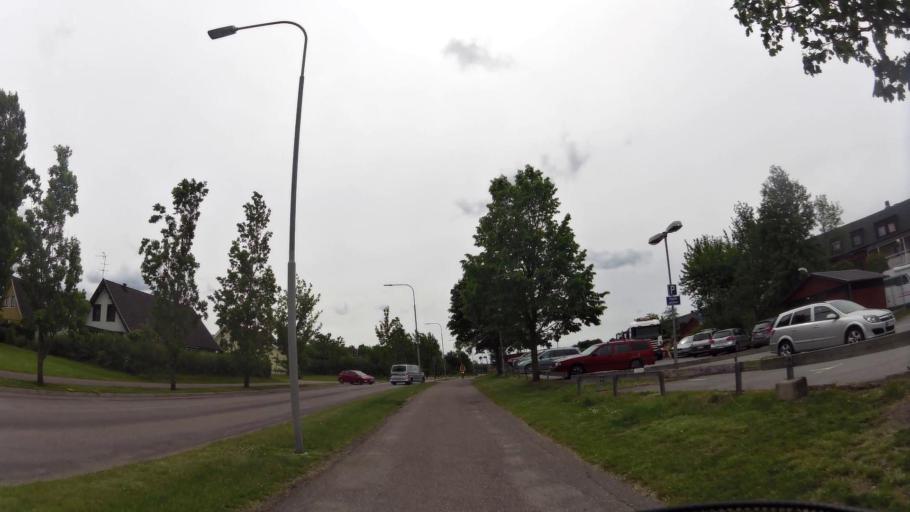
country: SE
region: OEstergoetland
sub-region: Linkopings Kommun
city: Linkoping
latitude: 58.3876
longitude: 15.5743
